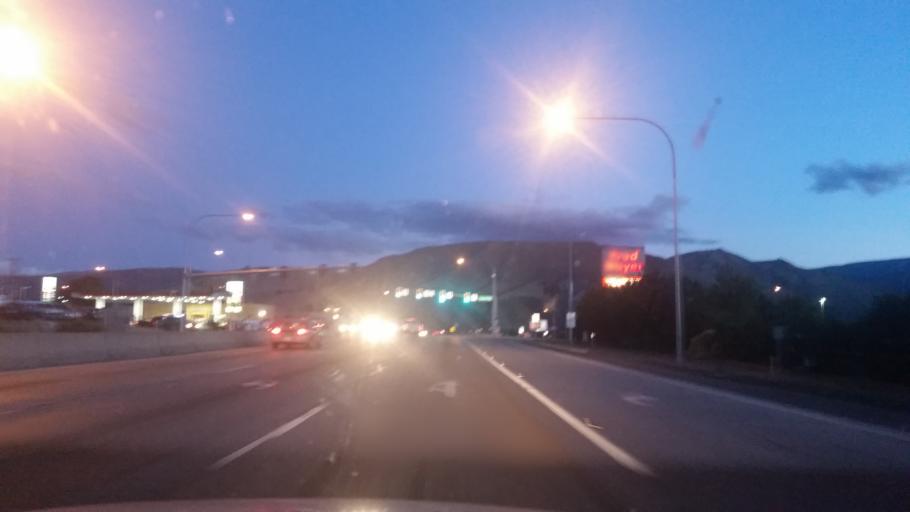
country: US
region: Washington
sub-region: Douglas County
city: East Wenatchee
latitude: 47.4070
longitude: -120.2898
